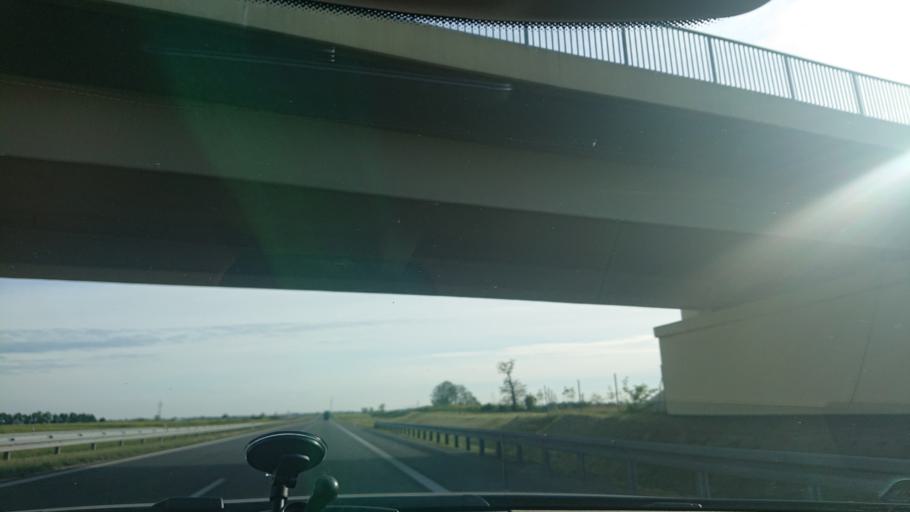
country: PL
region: Greater Poland Voivodeship
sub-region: Powiat gnieznienski
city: Gniezno
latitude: 52.5383
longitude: 17.5238
